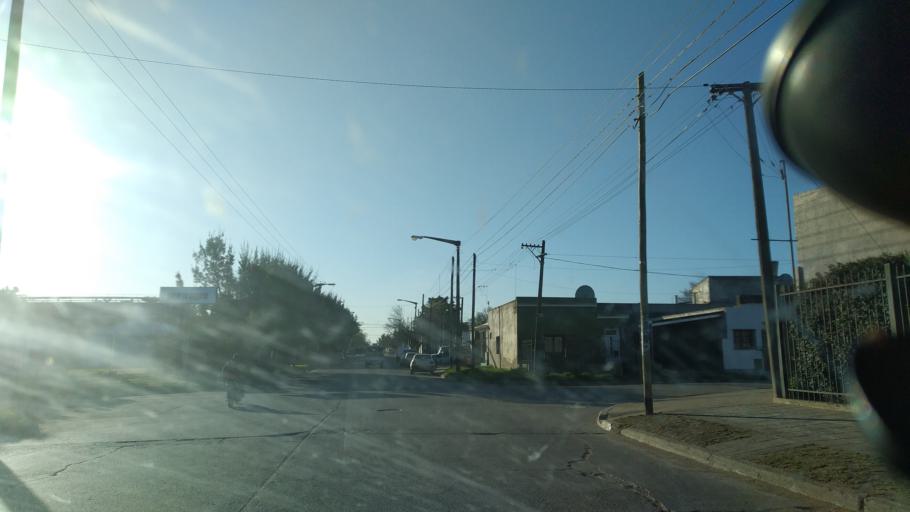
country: AR
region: Buenos Aires
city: Necochea
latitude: -38.5610
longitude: -58.7120
